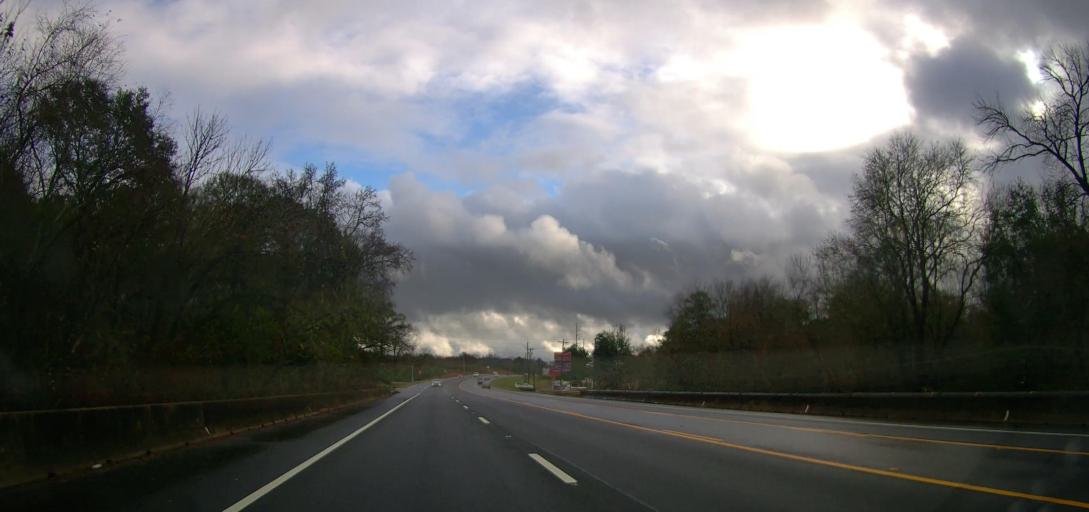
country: US
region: Georgia
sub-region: Clarke County
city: Athens
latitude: 33.9865
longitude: -83.3774
